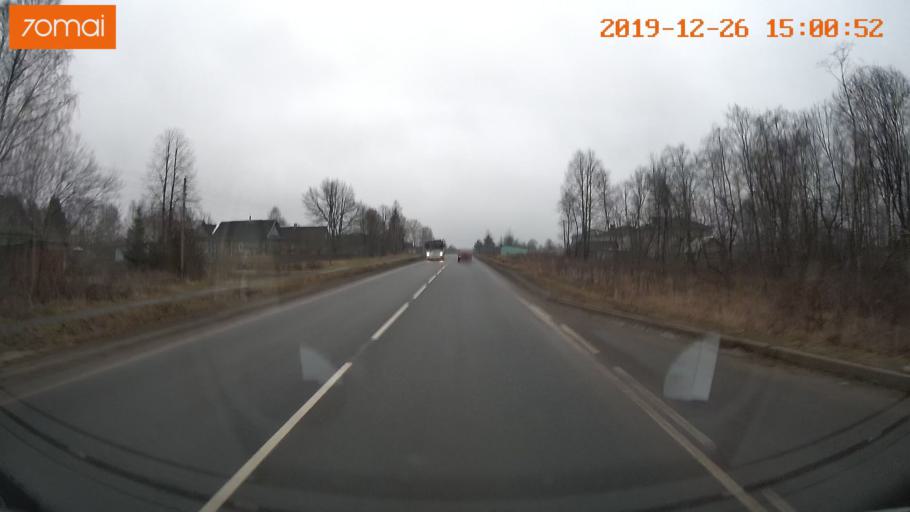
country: RU
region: Jaroslavl
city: Rybinsk
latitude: 58.2420
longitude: 38.8582
